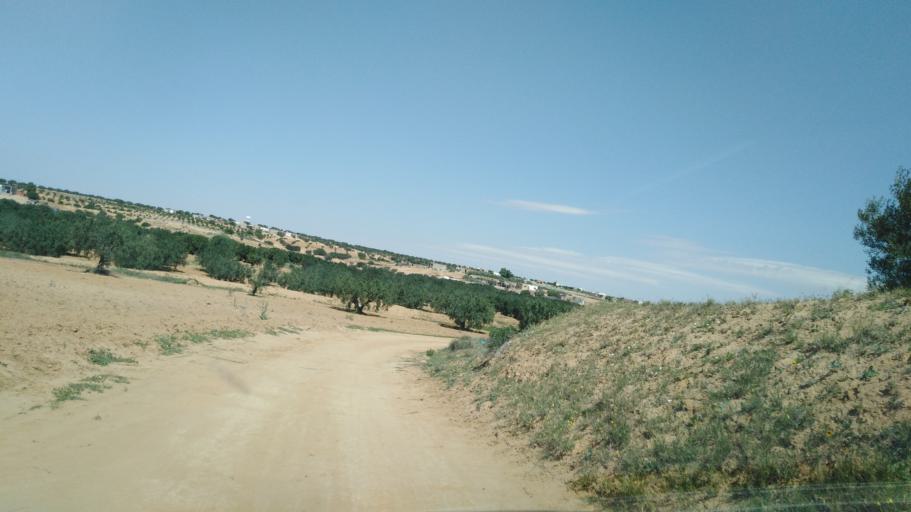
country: TN
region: Safaqis
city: Sfax
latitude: 34.7721
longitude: 10.5273
